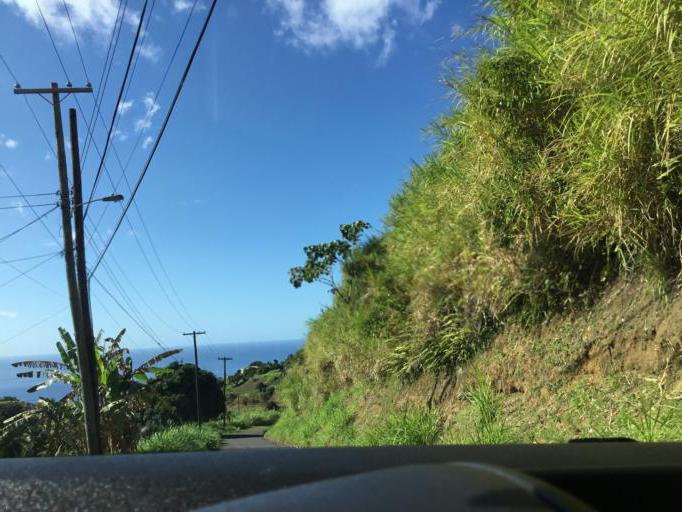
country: VC
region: Saint David
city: Chateaubelair
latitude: 13.2728
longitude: -61.2427
